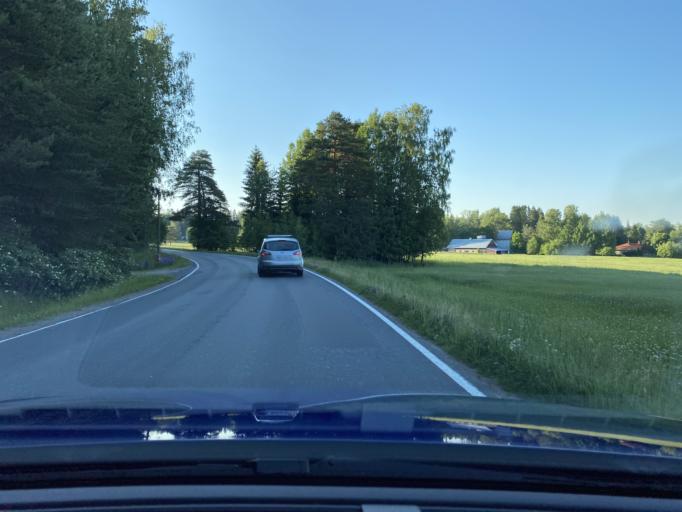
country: FI
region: Haeme
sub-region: Riihimaeki
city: Riihimaeki
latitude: 60.7229
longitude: 24.7039
